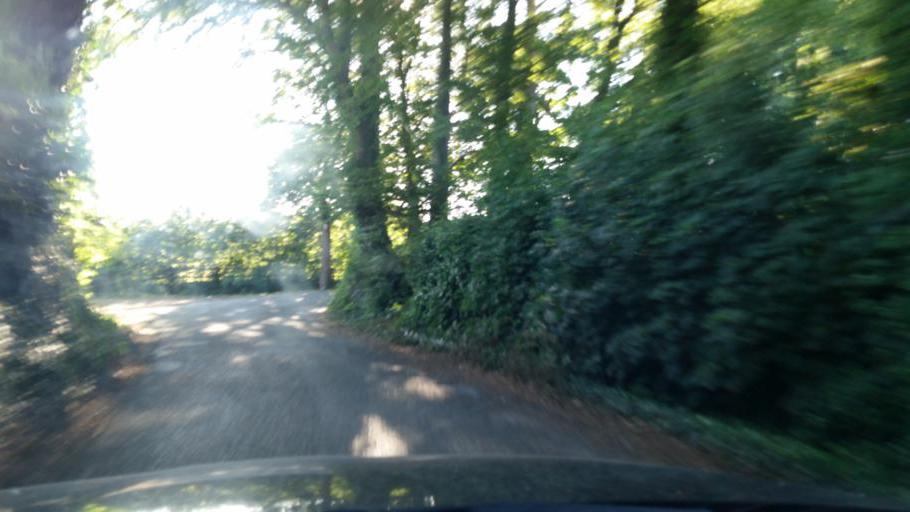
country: IE
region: Leinster
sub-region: Dublin City
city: Finglas
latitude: 53.4574
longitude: -6.3205
